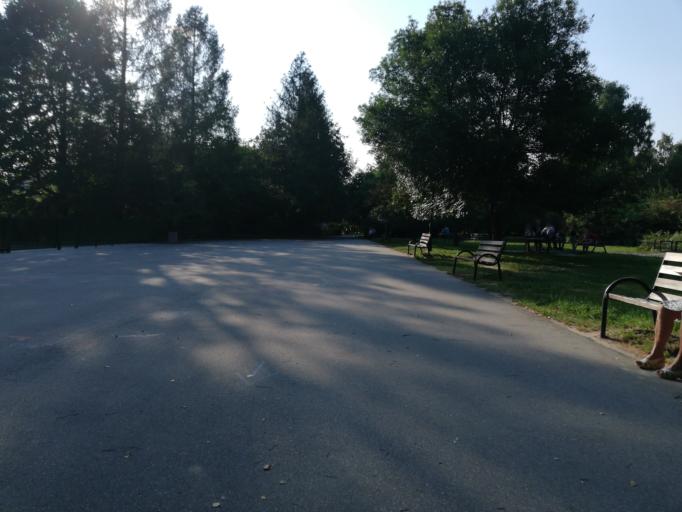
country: PL
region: Lesser Poland Voivodeship
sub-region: Krakow
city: Krakow
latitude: 50.0840
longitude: 20.0070
